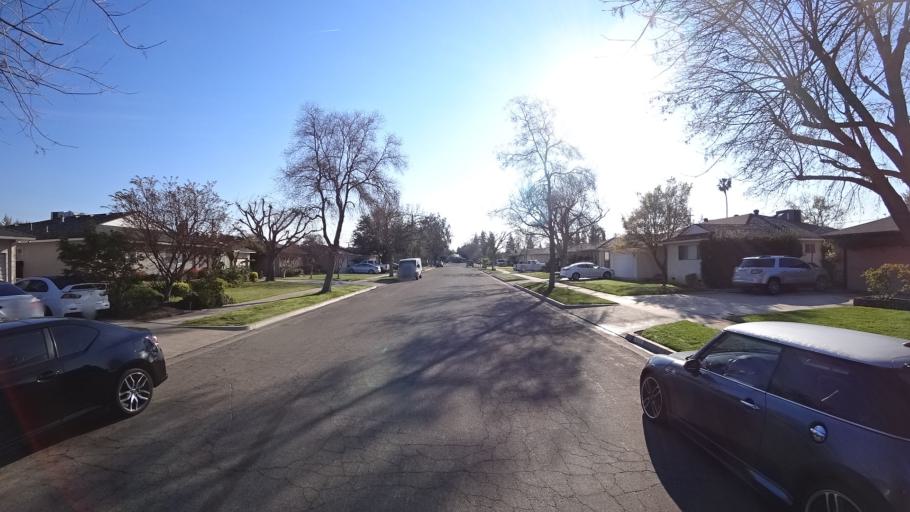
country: US
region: California
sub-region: Fresno County
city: Fresno
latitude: 36.8174
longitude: -119.7754
